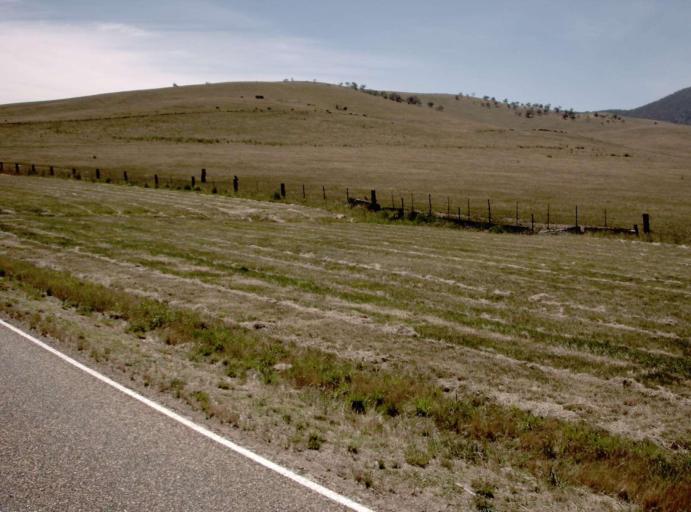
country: AU
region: Victoria
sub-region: Alpine
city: Mount Beauty
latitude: -36.9945
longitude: 147.6839
